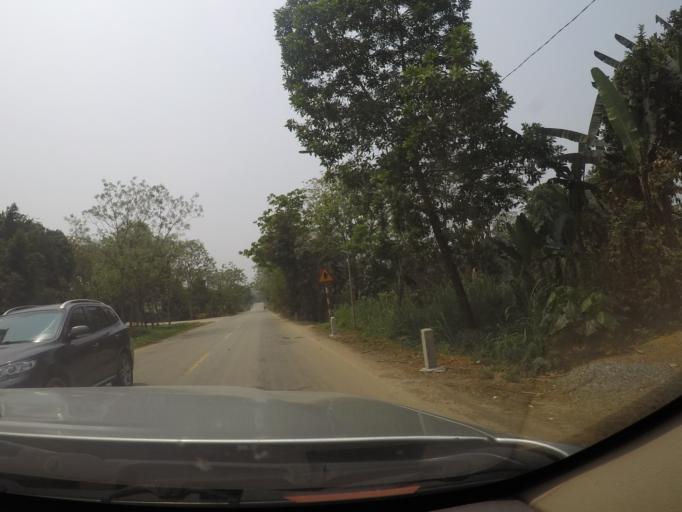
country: VN
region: Thanh Hoa
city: Thi Tran Thuong Xuan
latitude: 19.9400
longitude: 105.3973
